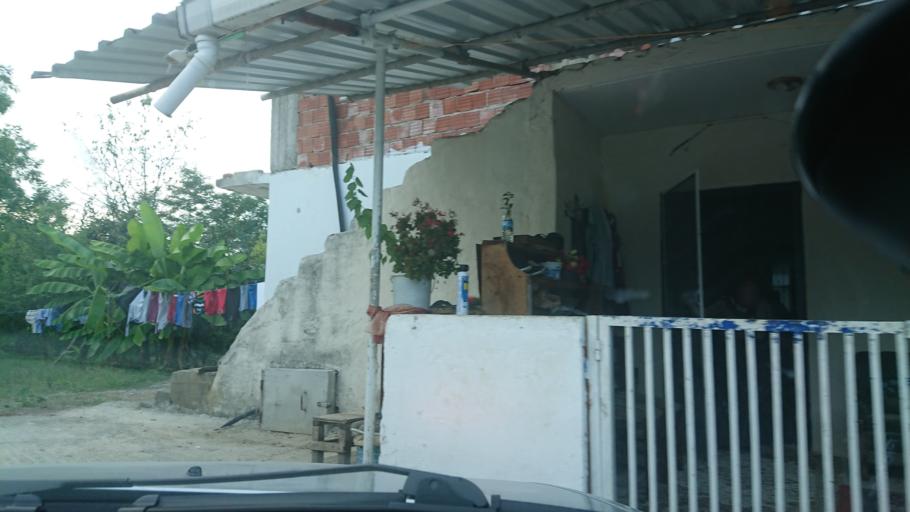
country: TR
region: Samsun
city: Dikbiyik
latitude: 41.1789
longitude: 36.5481
